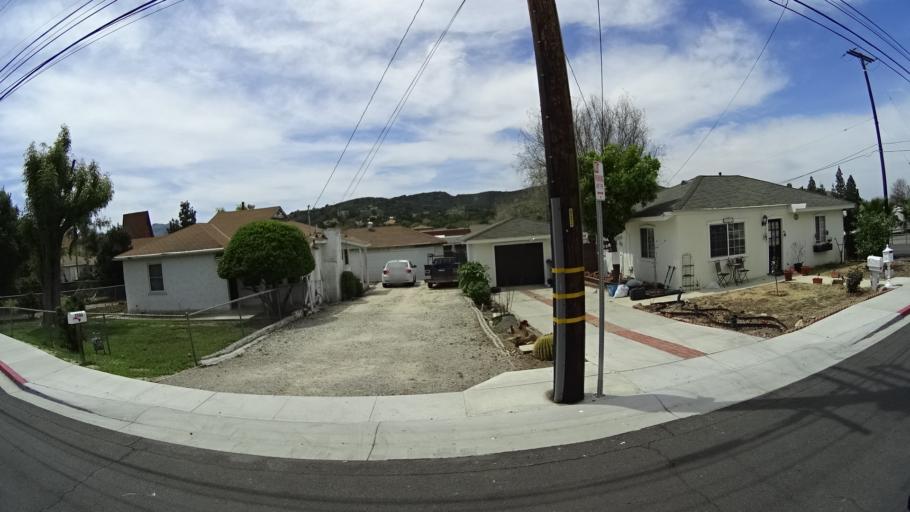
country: US
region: California
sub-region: Ventura County
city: Thousand Oaks
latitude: 34.1728
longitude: -118.8370
